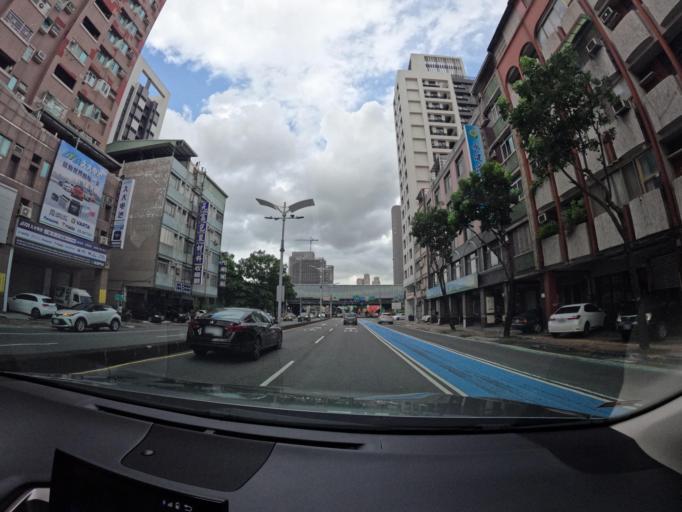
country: TW
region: Taiwan
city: Fengshan
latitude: 22.6376
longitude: 120.3358
